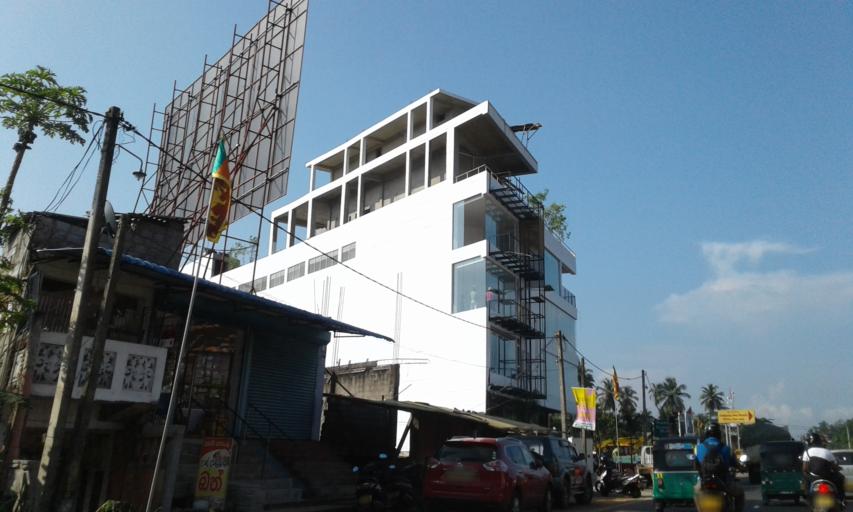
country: LK
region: Western
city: Gampaha
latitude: 7.0255
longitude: 79.9789
